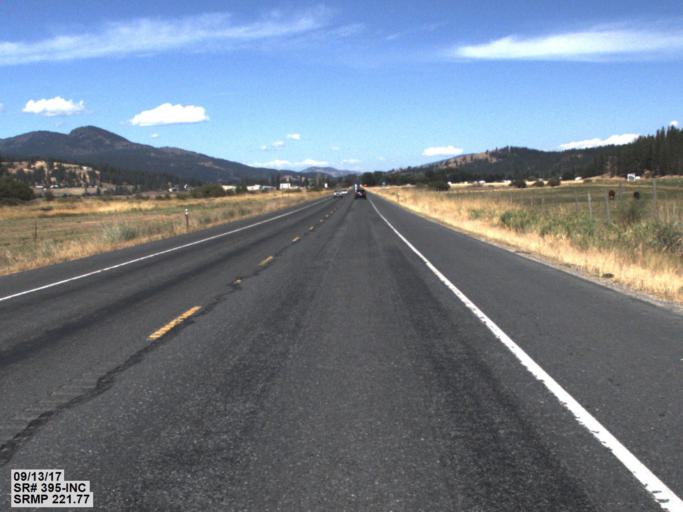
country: US
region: Washington
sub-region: Stevens County
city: Colville
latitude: 48.4395
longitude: -117.8658
